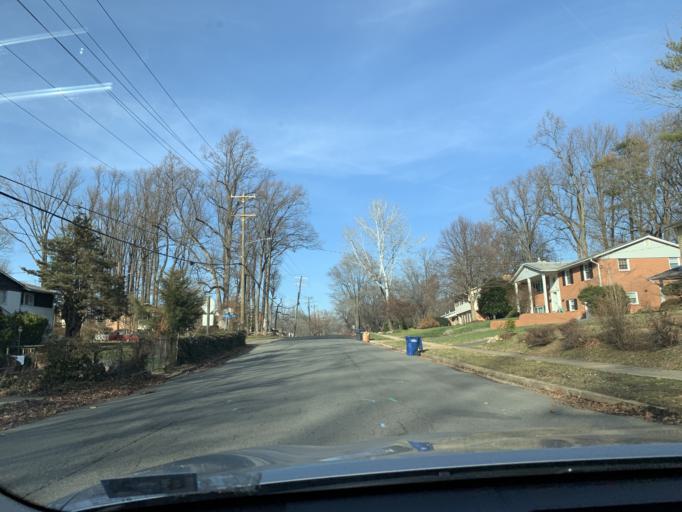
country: US
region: Virginia
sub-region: Fairfax County
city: Jefferson
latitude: 38.8504
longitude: -77.1853
